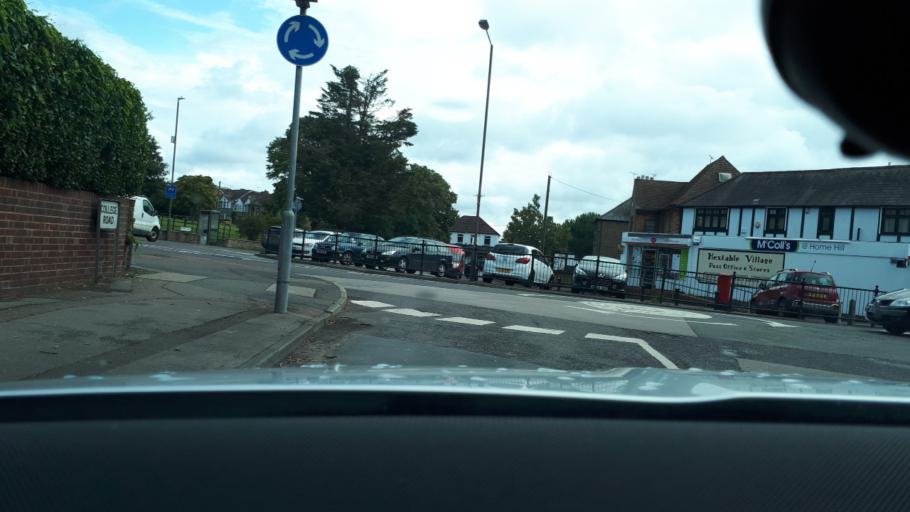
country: GB
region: England
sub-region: Kent
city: Swanley
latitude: 51.4111
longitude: 0.1817
